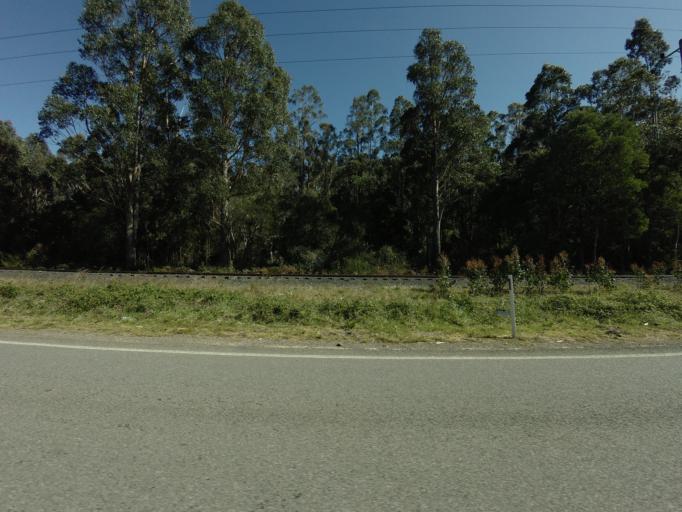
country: AU
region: Tasmania
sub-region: Derwent Valley
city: New Norfolk
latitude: -42.7176
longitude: 146.6891
